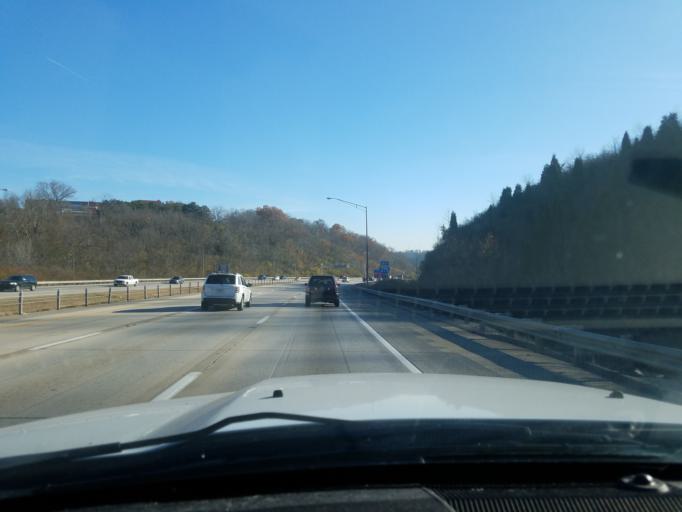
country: US
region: Kentucky
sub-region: Kenton County
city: Lakeside Park
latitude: 39.0261
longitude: -84.5561
